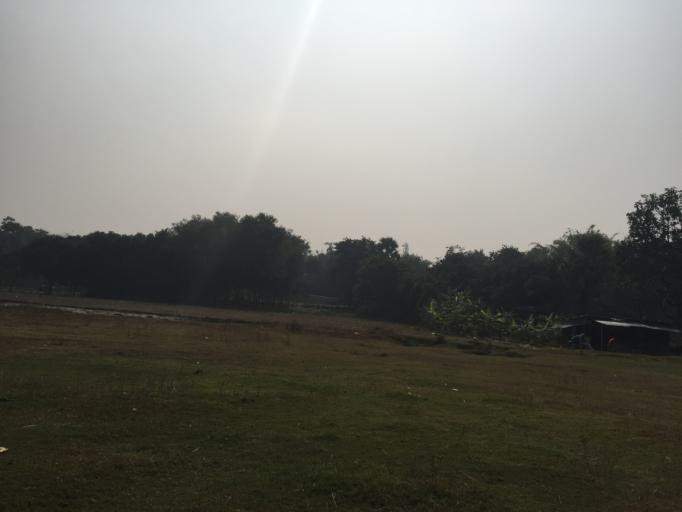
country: BD
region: Dhaka
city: Tungi
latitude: 23.8657
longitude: 90.3150
